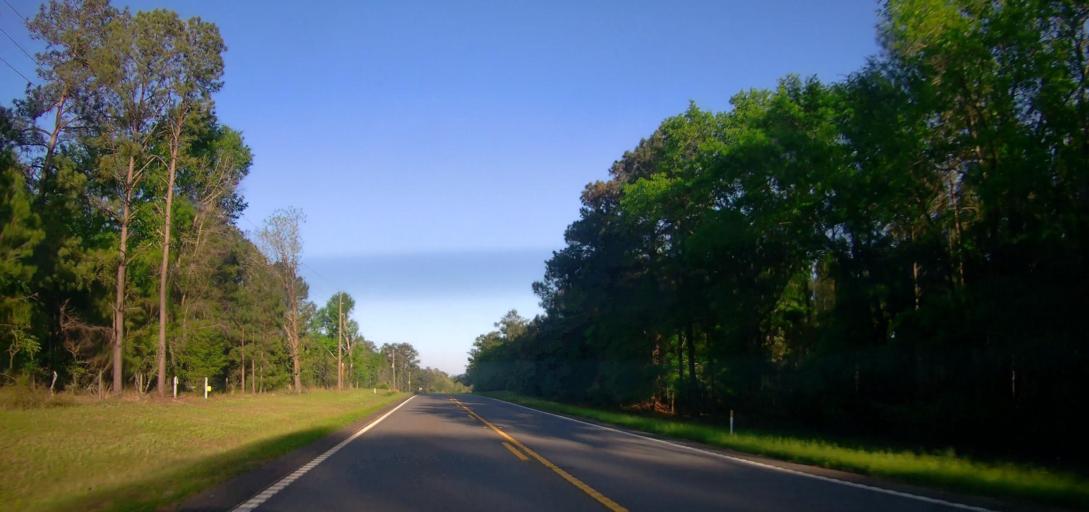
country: US
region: Georgia
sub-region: Schley County
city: Ellaville
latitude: 32.3300
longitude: -84.3372
